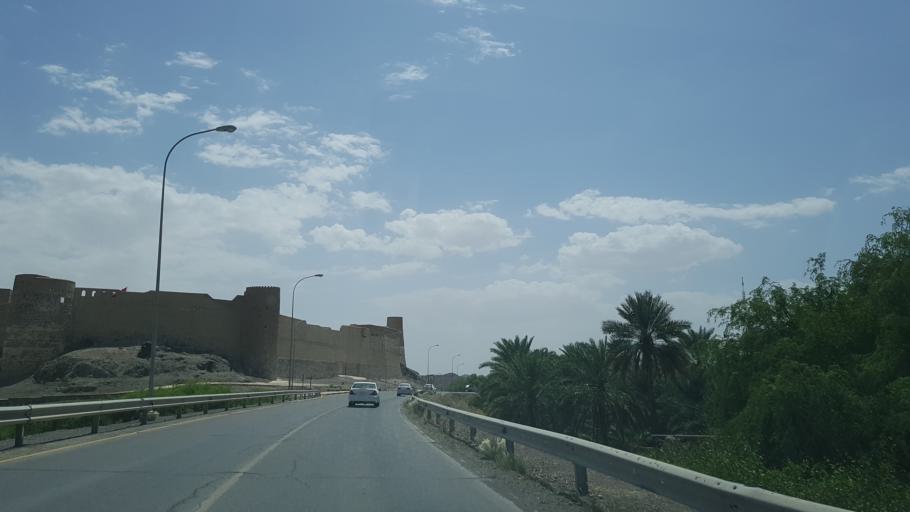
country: OM
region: Muhafazat ad Dakhiliyah
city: Bahla'
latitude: 22.9662
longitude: 57.3016
